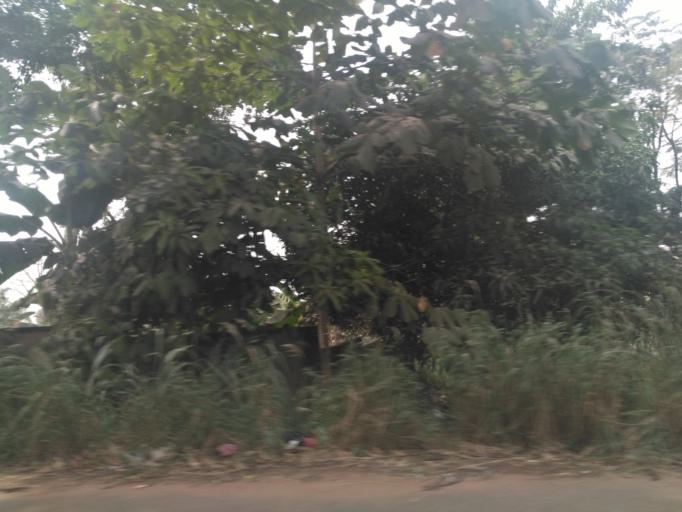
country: GH
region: Ashanti
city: Kumasi
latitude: 6.6898
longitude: -1.6335
